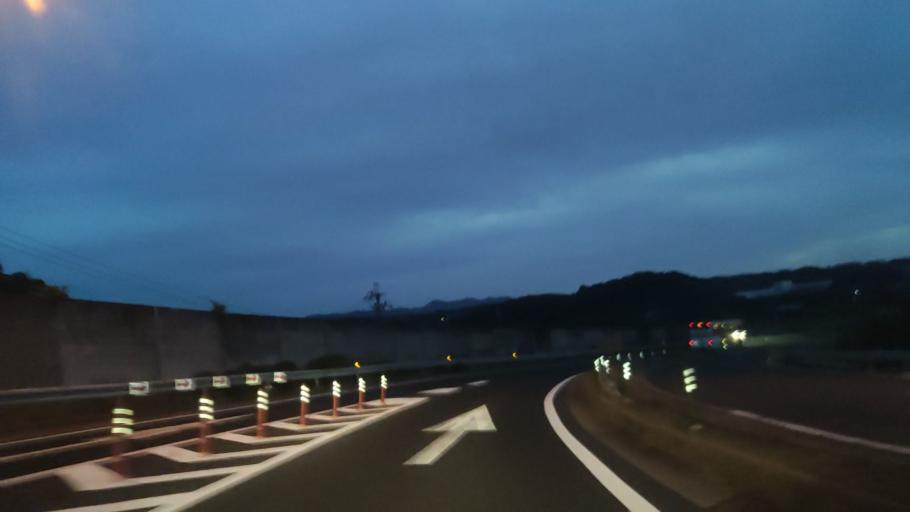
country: JP
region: Hyogo
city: Sandacho
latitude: 34.8879
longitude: 135.1182
